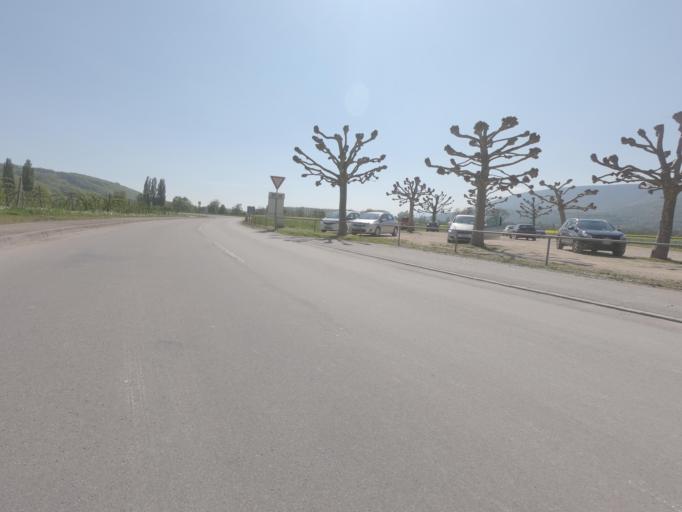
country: CH
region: Neuchatel
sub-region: Neuchatel District
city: Le Landeron
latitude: 47.0484
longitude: 7.0649
